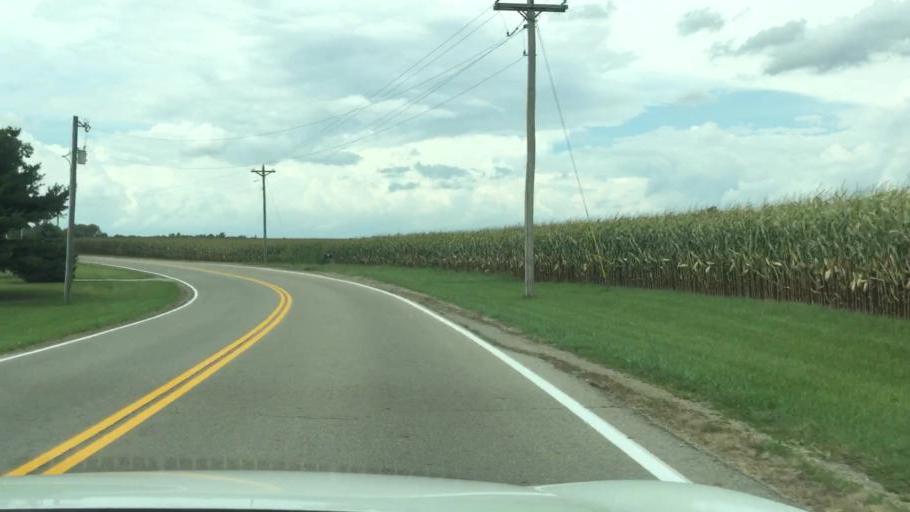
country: US
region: Ohio
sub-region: Champaign County
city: Urbana
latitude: 40.0698
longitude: -83.7116
